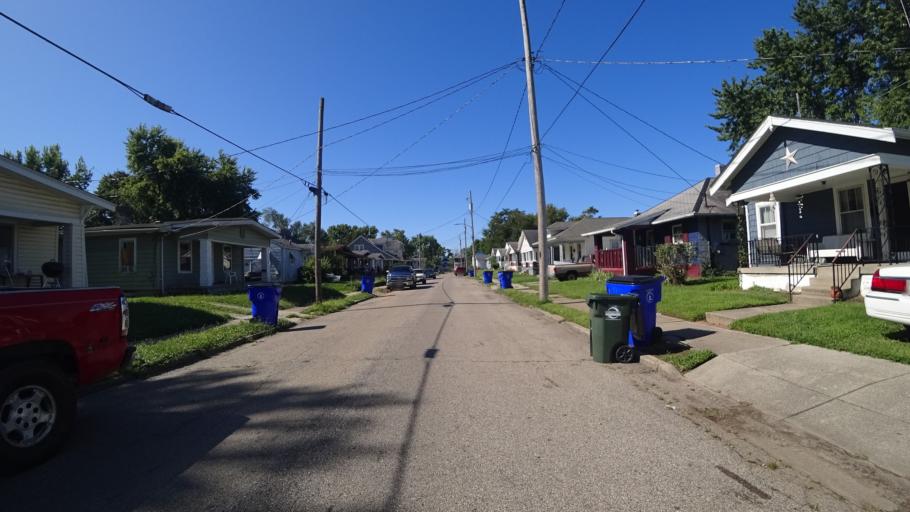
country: US
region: Ohio
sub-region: Butler County
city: Hamilton
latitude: 39.3980
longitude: -84.5437
